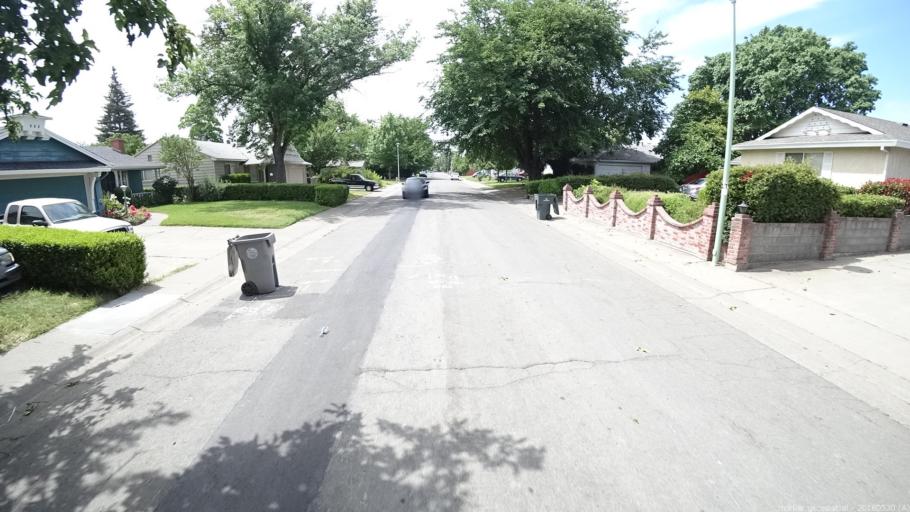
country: US
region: California
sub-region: Sacramento County
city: Sacramento
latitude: 38.6149
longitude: -121.4812
